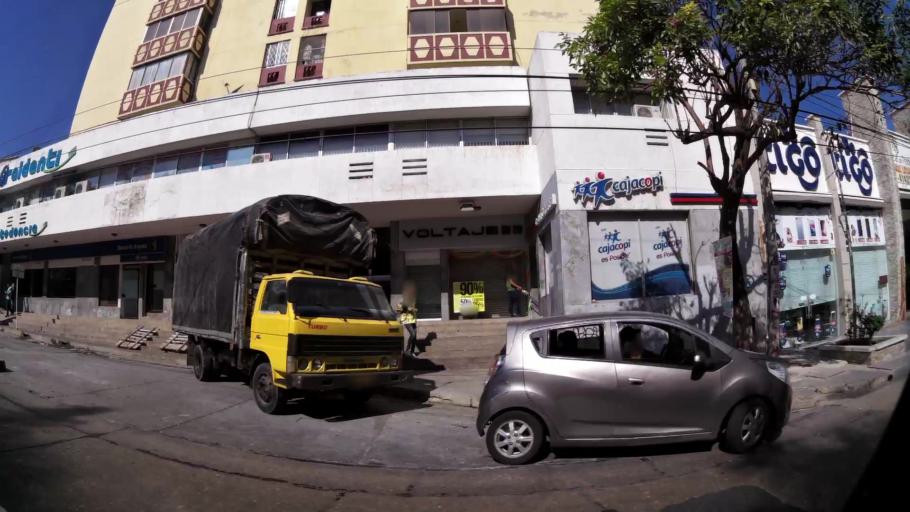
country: CO
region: Atlantico
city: Barranquilla
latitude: 10.9893
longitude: -74.7894
